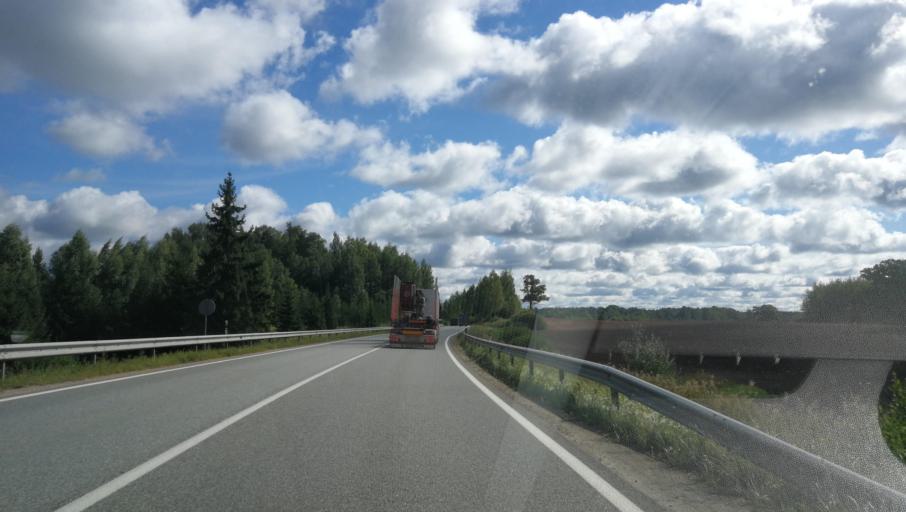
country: LV
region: Ligatne
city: Ligatne
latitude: 57.2040
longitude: 25.1371
